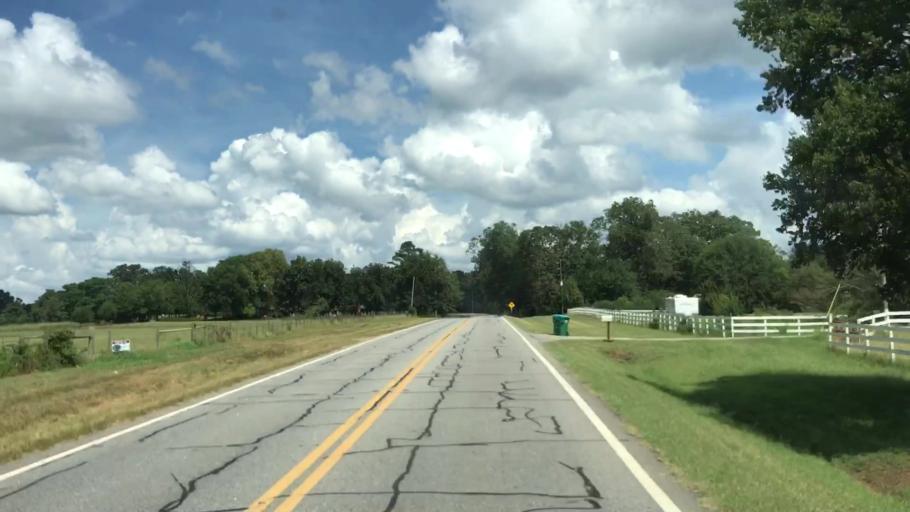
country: US
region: Georgia
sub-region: Oconee County
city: Watkinsville
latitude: 33.7432
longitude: -83.3024
